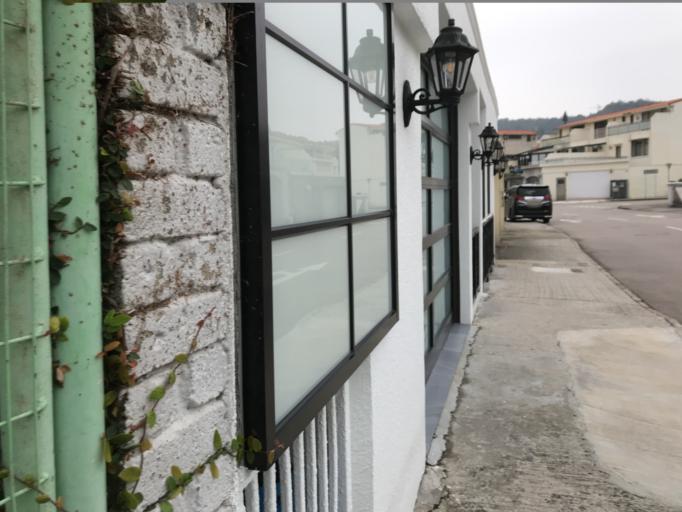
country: HK
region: Tai Po
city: Tai Po
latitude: 22.4659
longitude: 114.1536
